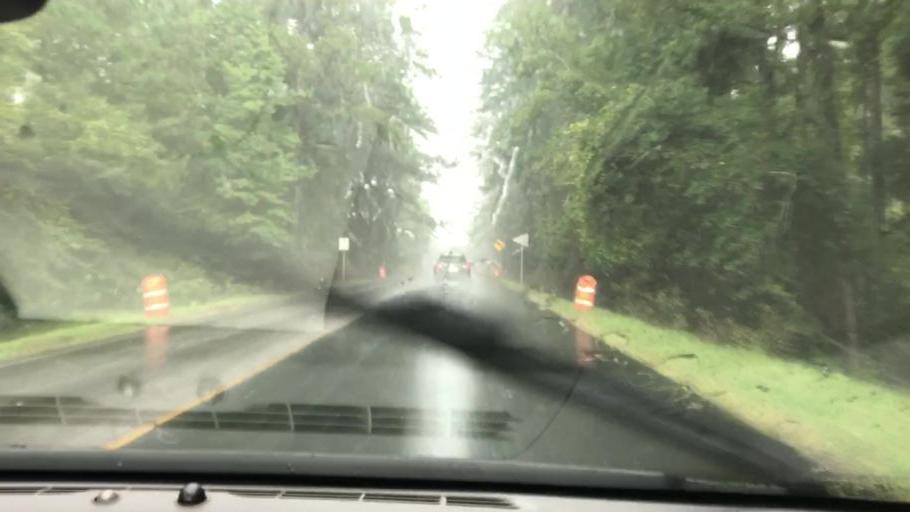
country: US
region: Georgia
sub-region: Clay County
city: Fort Gaines
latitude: 31.5508
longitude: -85.0188
